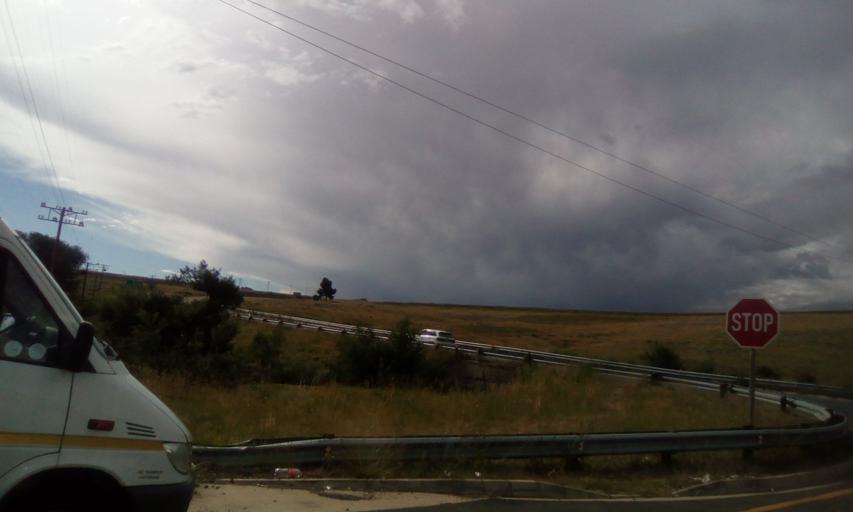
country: ZA
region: Orange Free State
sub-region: Thabo Mofutsanyana District Municipality
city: Ladybrand
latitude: -29.2134
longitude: 27.4529
